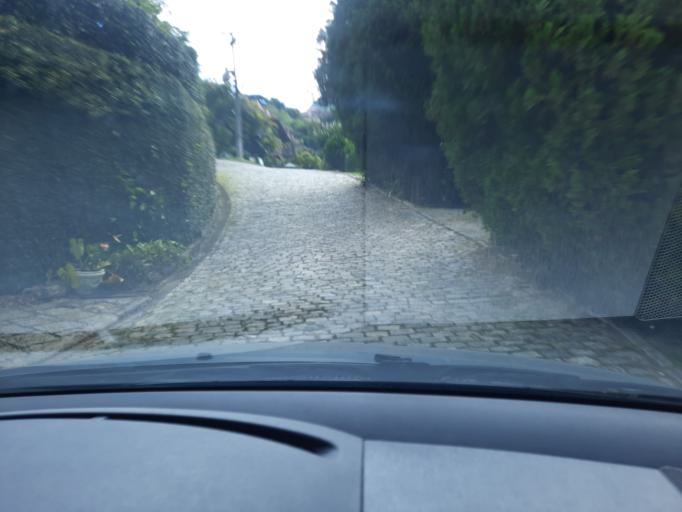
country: BR
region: Rio de Janeiro
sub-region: Petropolis
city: Petropolis
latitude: -22.4411
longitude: -43.1730
